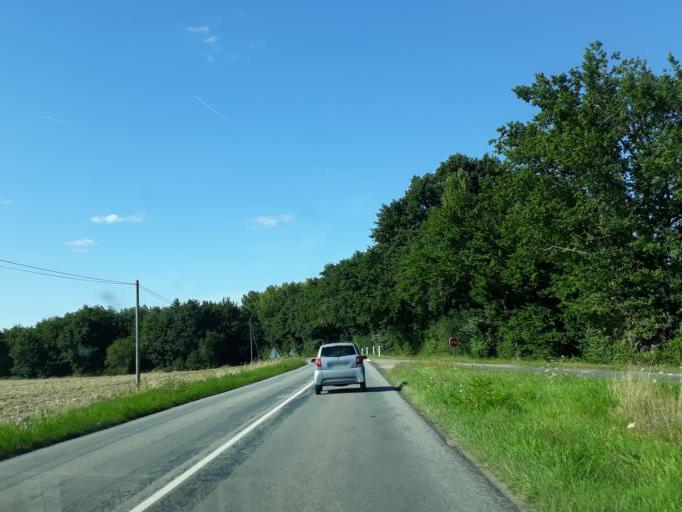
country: FR
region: Centre
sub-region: Departement du Loiret
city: Saint-Benoit-sur-Loire
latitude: 47.8384
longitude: 2.2683
